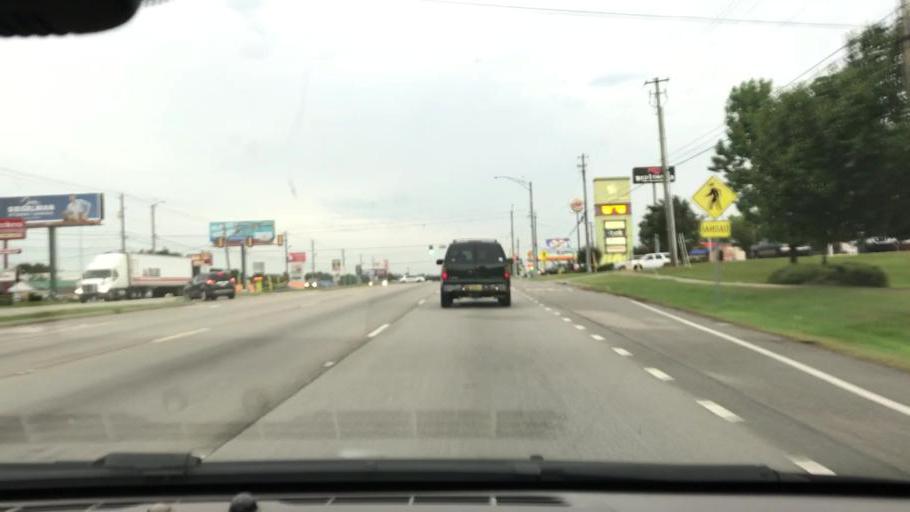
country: US
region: Alabama
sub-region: Houston County
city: Dothan
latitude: 31.2514
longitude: -85.4269
